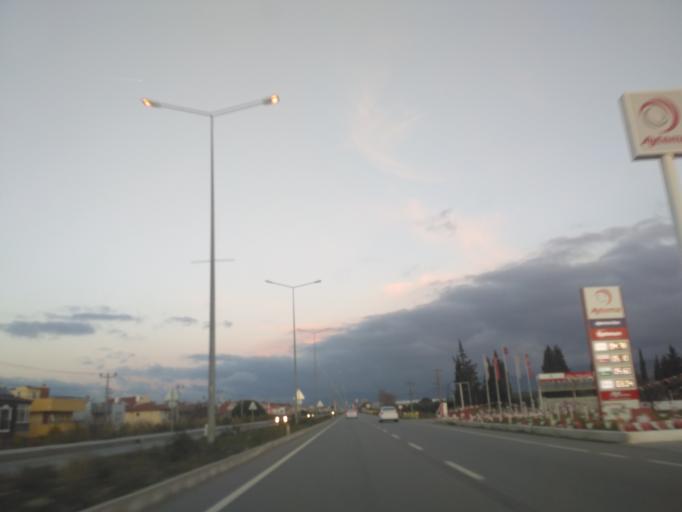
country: TR
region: Balikesir
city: Burhaniye
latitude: 39.4843
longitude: 26.9363
